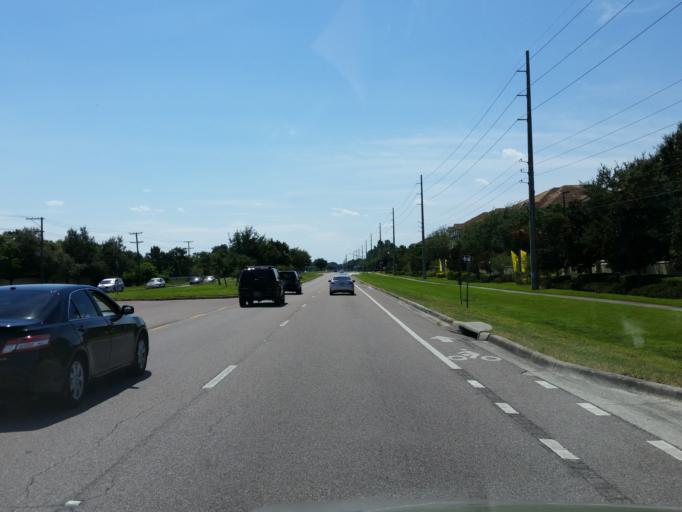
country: US
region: Florida
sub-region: Hillsborough County
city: Brandon
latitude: 27.9196
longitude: -82.3188
